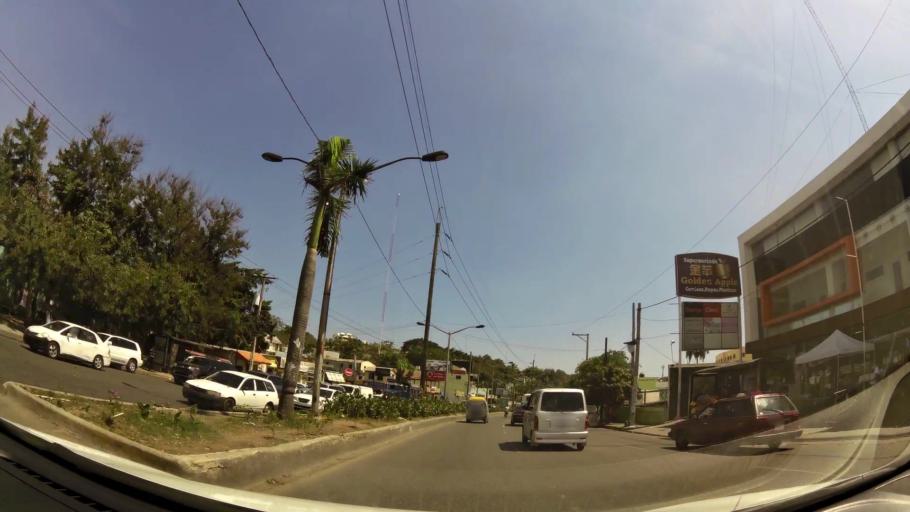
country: DO
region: Santo Domingo
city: Santo Domingo Oeste
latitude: 18.4771
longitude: -69.9963
